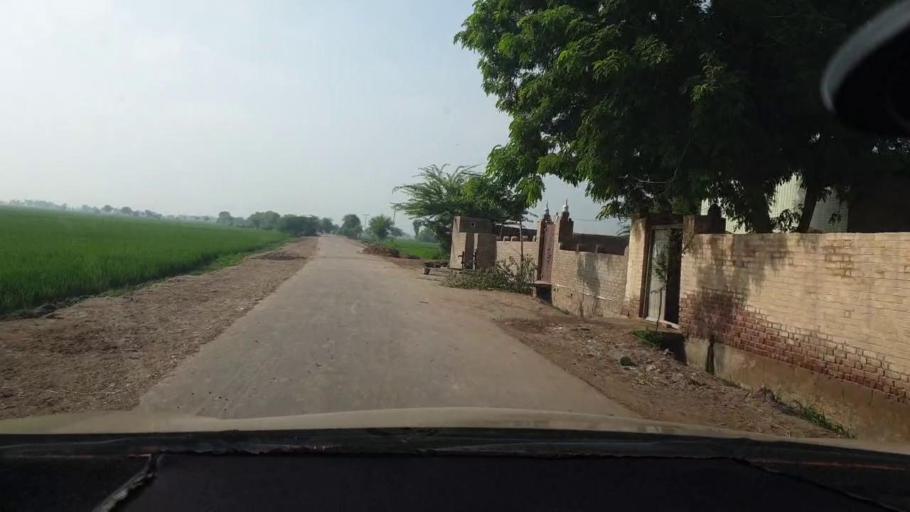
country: PK
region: Sindh
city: Goth Garelo
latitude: 27.4855
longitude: 68.0126
